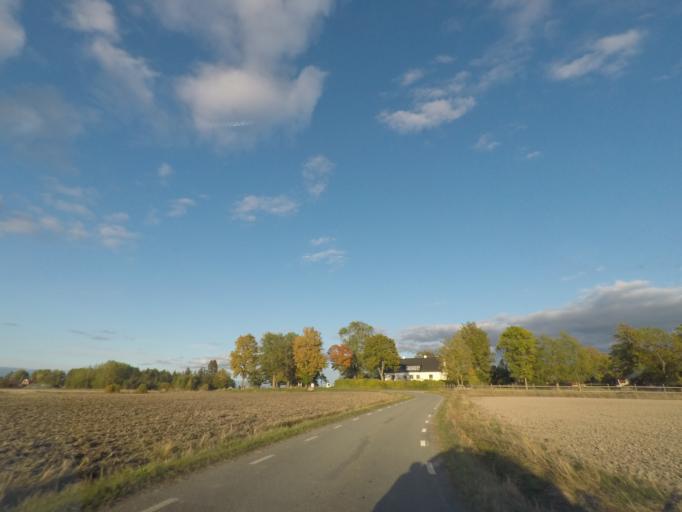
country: SE
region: Vaestmanland
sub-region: Kungsors Kommun
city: Kungsoer
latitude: 59.5222
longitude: 16.1157
